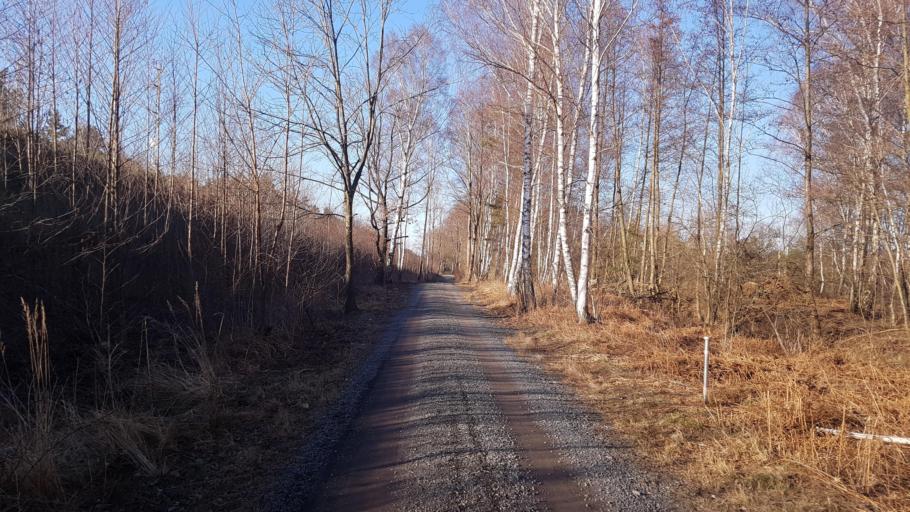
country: DE
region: Brandenburg
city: Hohenleipisch
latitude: 51.5084
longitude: 13.5769
